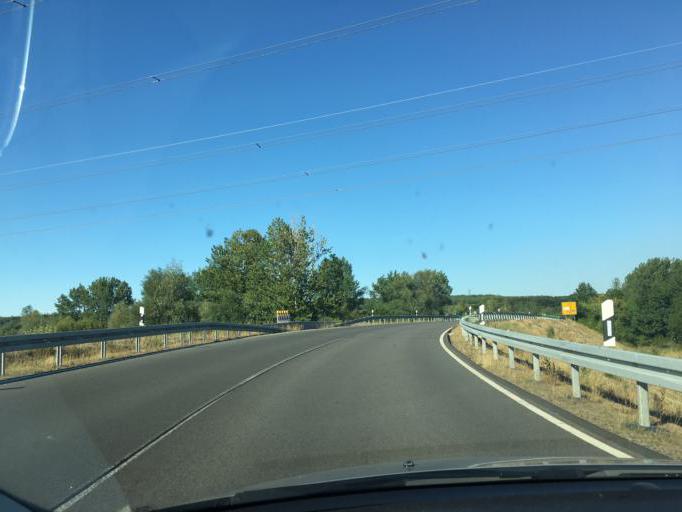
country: DE
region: Saxony
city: Espenhain
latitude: 51.1732
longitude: 12.4943
